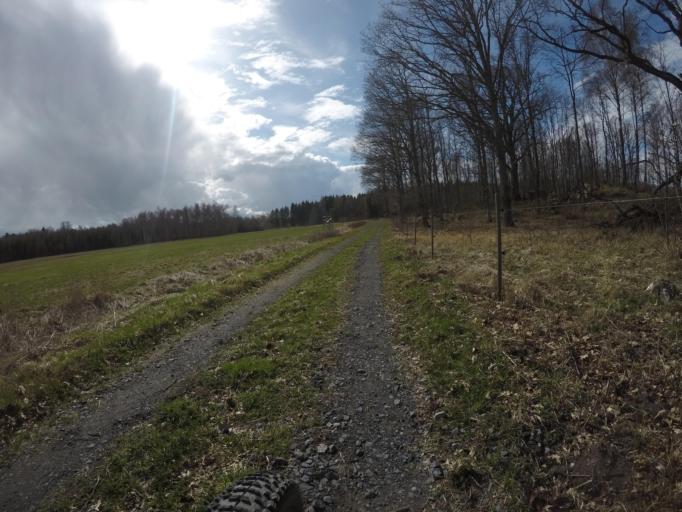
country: SE
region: Vaestmanland
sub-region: Kungsors Kommun
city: Kungsoer
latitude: 59.2741
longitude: 16.1519
